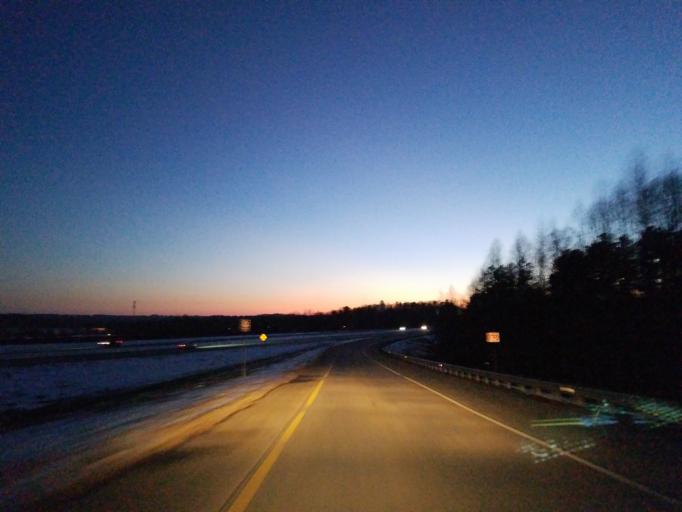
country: US
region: Georgia
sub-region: Cherokee County
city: Ball Ground
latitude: 34.3001
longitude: -84.4264
